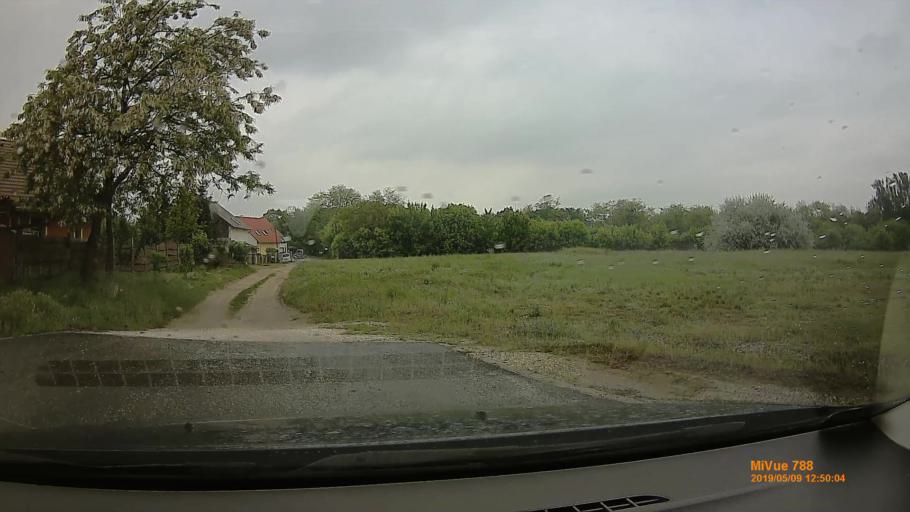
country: HU
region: Budapest
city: Budapest XVI. keruelet
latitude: 47.5402
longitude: 19.1769
